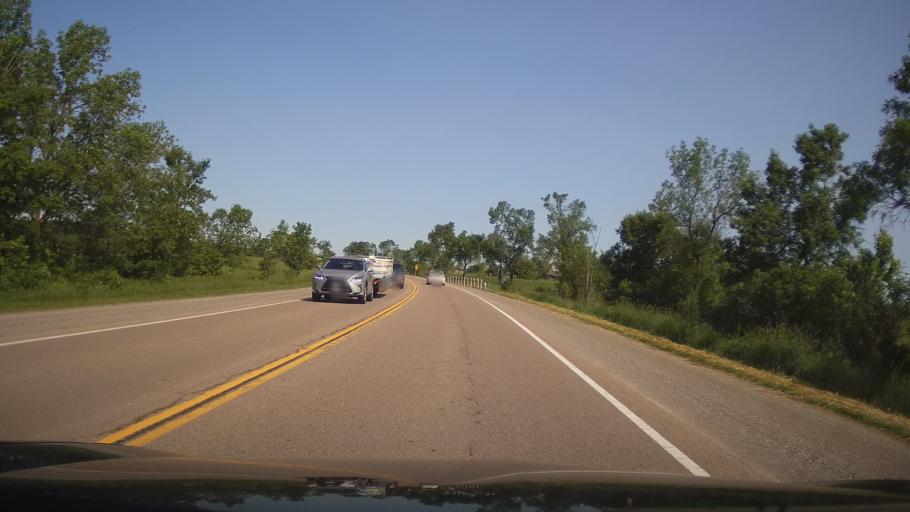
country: CA
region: Ontario
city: Omemee
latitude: 44.3431
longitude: -78.7666
